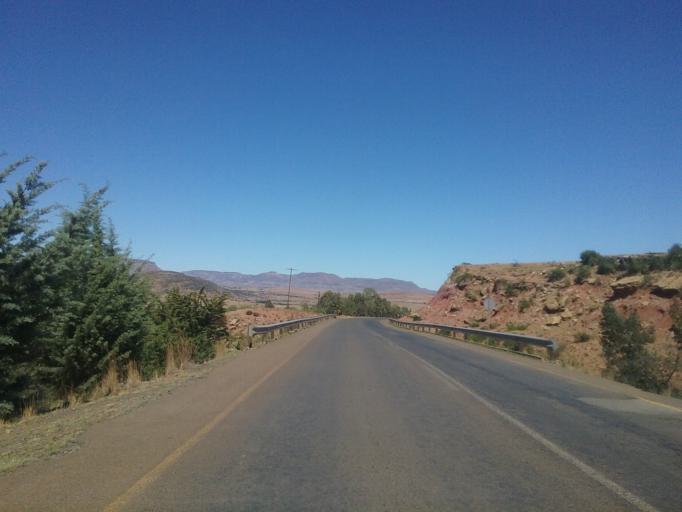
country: LS
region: Quthing
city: Quthing
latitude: -30.3886
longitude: 27.6199
